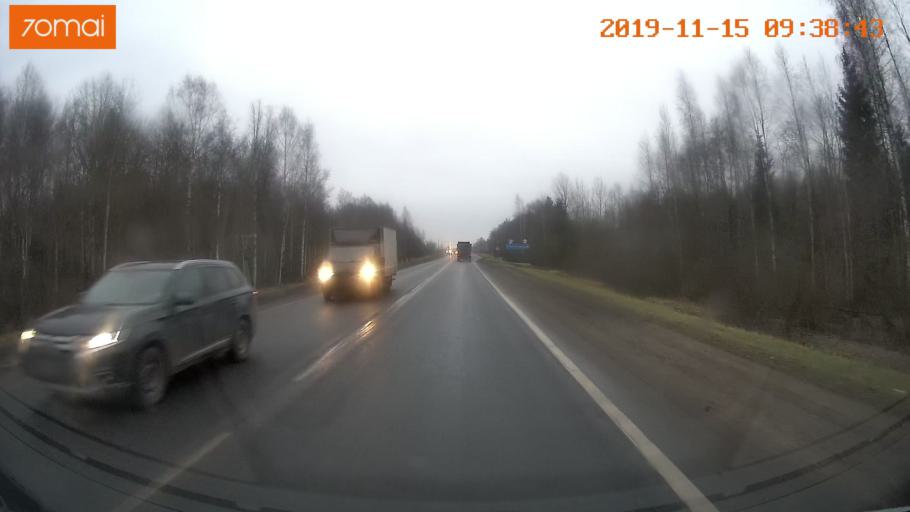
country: RU
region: Vologda
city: Sheksna
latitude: 59.2294
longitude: 38.4608
